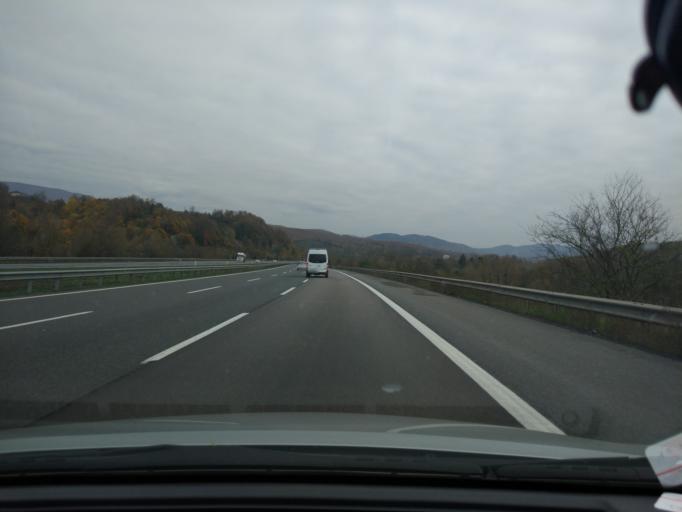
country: TR
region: Sakarya
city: Hendek
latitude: 40.7728
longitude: 30.7833
